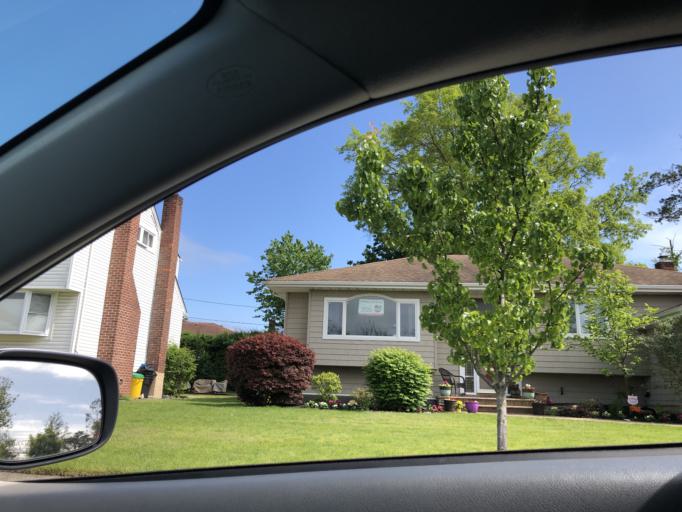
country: US
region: New York
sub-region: Nassau County
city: South Valley Stream
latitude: 40.6485
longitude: -73.7252
